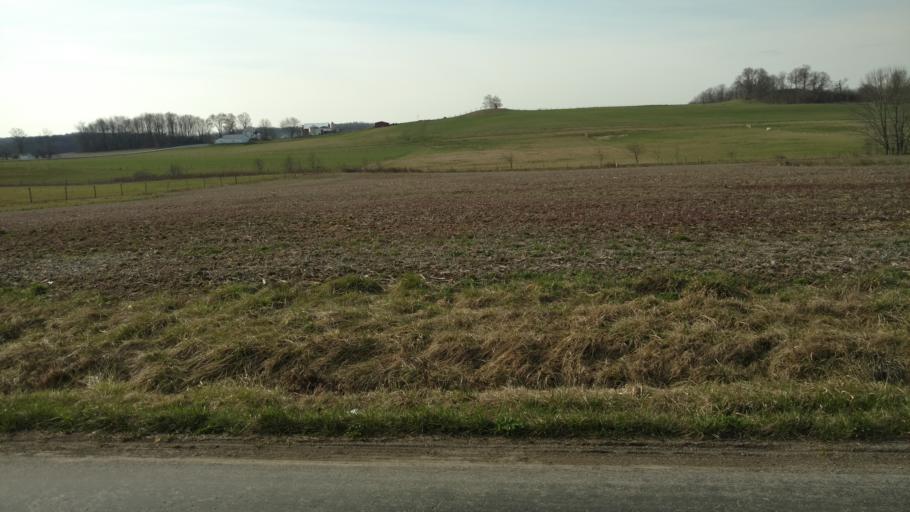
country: US
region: Ohio
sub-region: Knox County
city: Fredericktown
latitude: 40.5255
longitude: -82.6061
